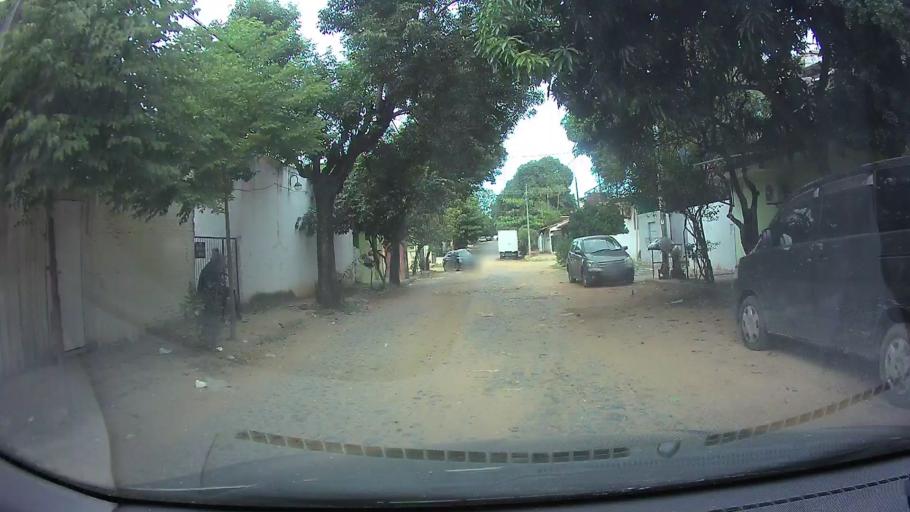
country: PY
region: Central
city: Lambare
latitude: -25.3173
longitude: -57.5976
